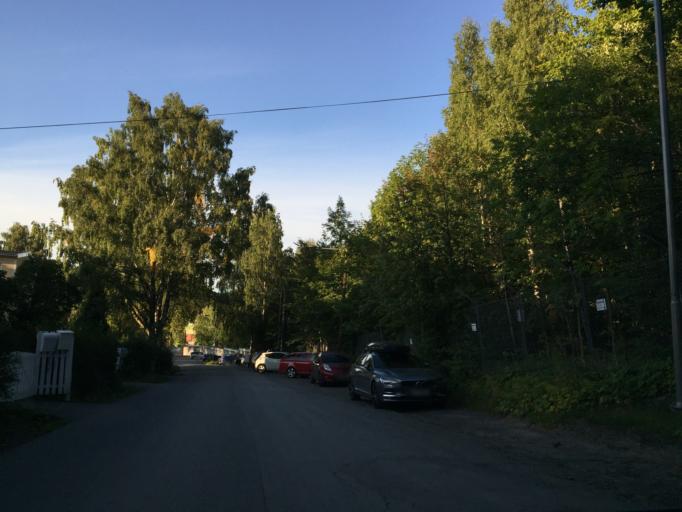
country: NO
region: Akershus
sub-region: Baerum
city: Lysaker
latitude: 59.9023
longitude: 10.6143
